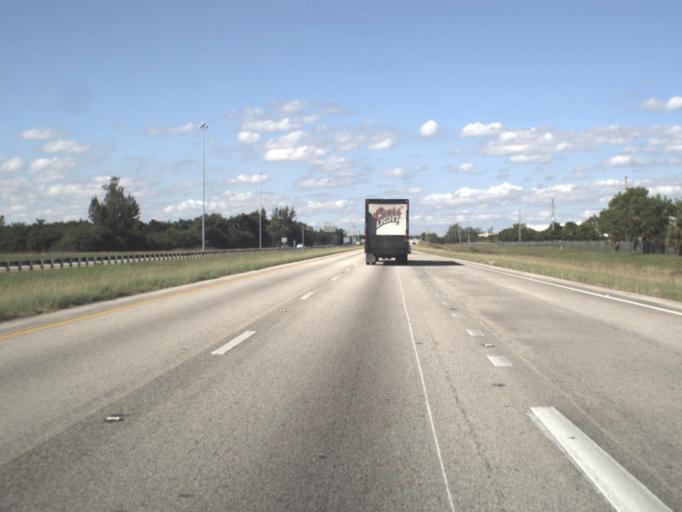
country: US
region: Florida
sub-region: Miami-Dade County
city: Country Club
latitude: 25.9710
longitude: -80.2967
